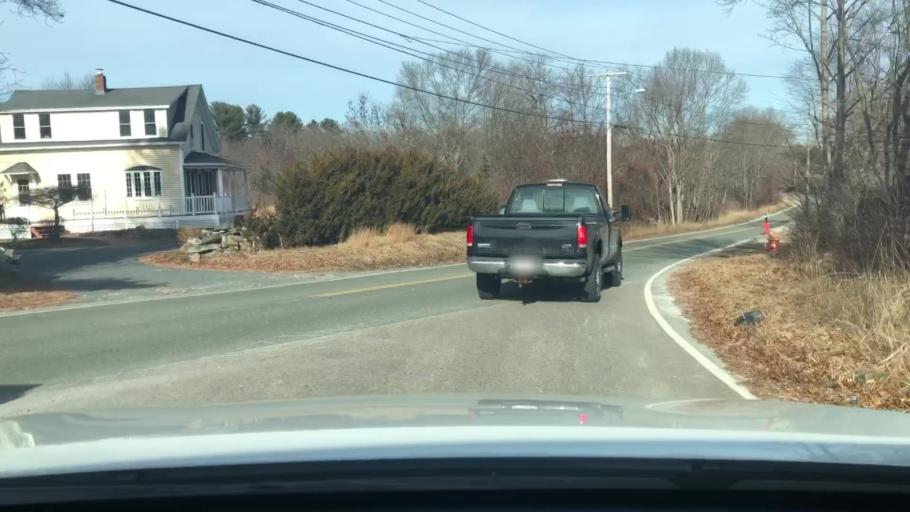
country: US
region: Massachusetts
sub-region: Worcester County
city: Blackstone
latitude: 42.0610
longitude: -71.5270
